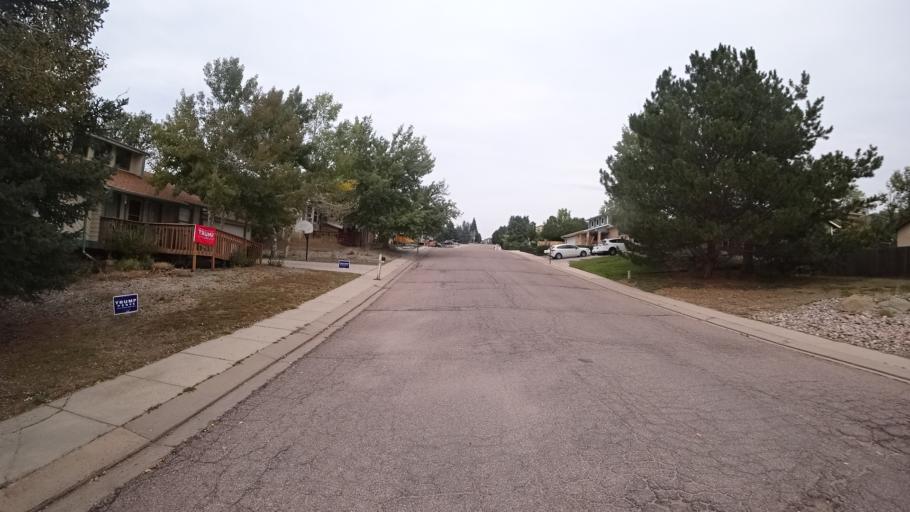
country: US
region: Colorado
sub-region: El Paso County
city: Cimarron Hills
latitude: 38.9034
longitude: -104.7242
